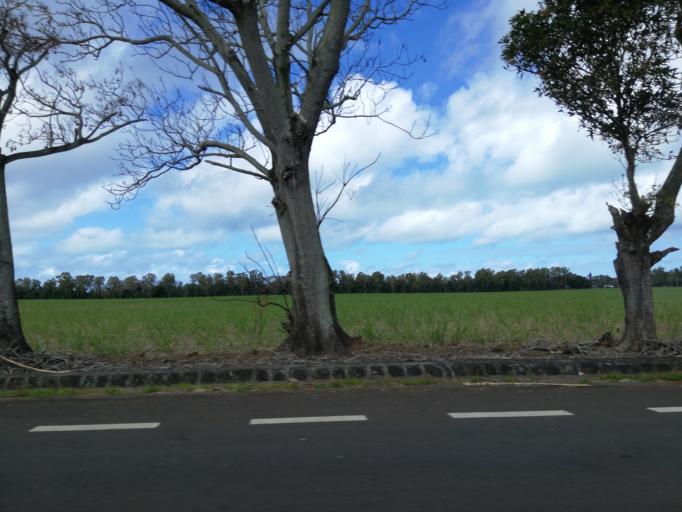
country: MU
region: Grand Port
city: Mahebourg
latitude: -20.3797
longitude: 57.6983
